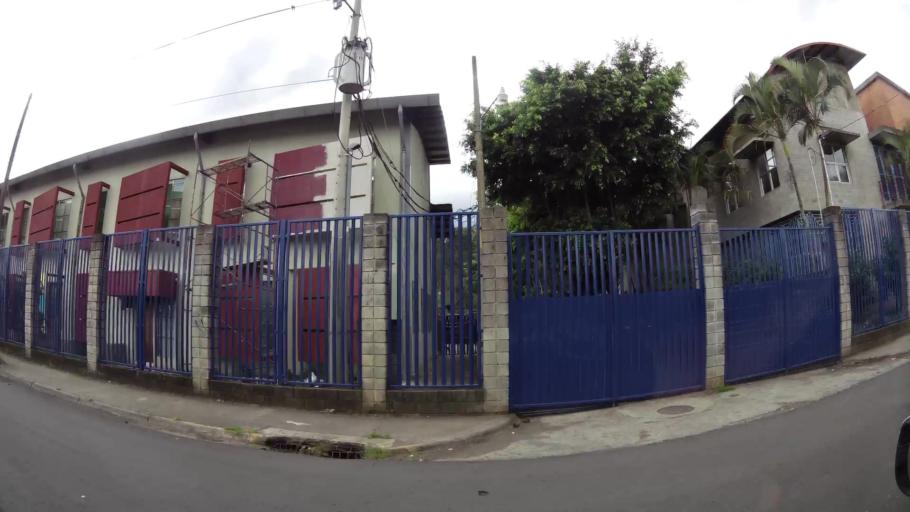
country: CR
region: San Jose
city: San Juan de Dios
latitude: 9.8901
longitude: -84.0868
